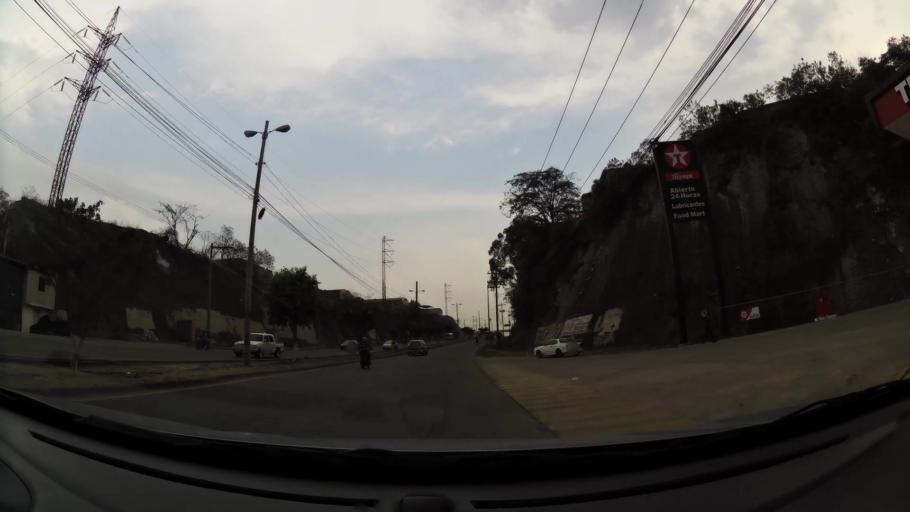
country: HN
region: Francisco Morazan
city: El Lolo
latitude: 14.0949
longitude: -87.2395
